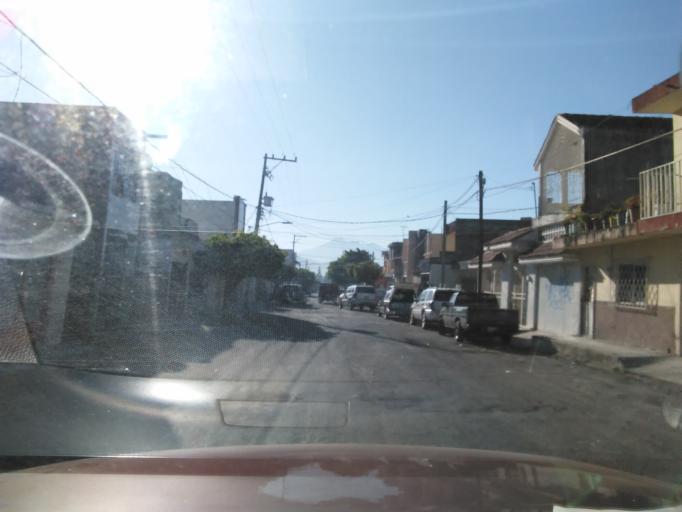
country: MX
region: Nayarit
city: Tepic
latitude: 21.5217
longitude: -104.9045
